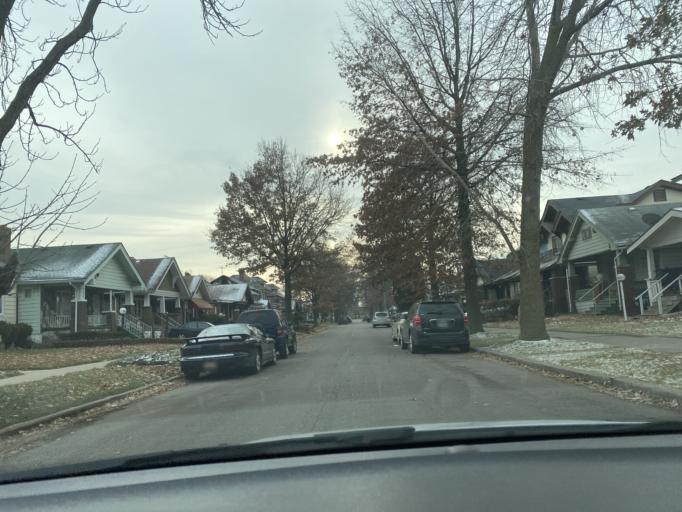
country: US
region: Michigan
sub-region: Wayne County
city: Highland Park
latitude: 42.3705
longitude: -83.1248
